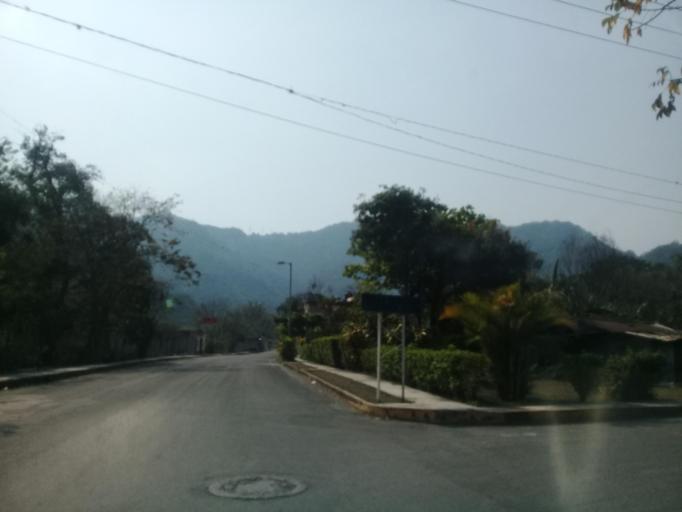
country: MX
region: Veracruz
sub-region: Ixtaczoquitlan
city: Campo Chico
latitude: 18.8341
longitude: -97.0255
